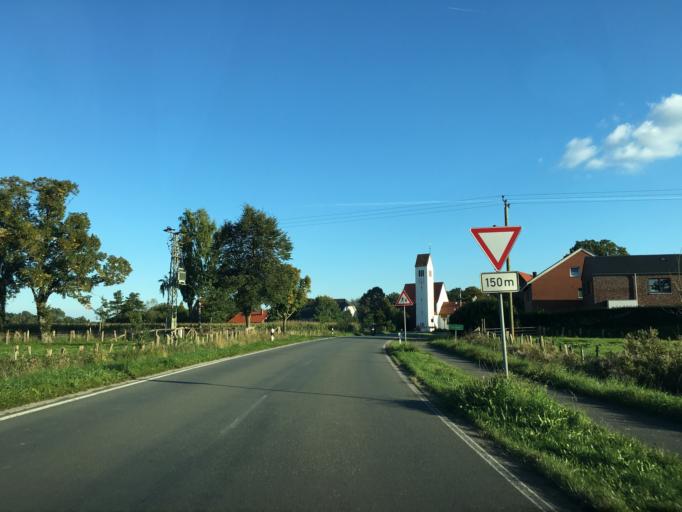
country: DE
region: North Rhine-Westphalia
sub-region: Regierungsbezirk Munster
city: Nordwalde
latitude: 52.0429
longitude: 7.5350
